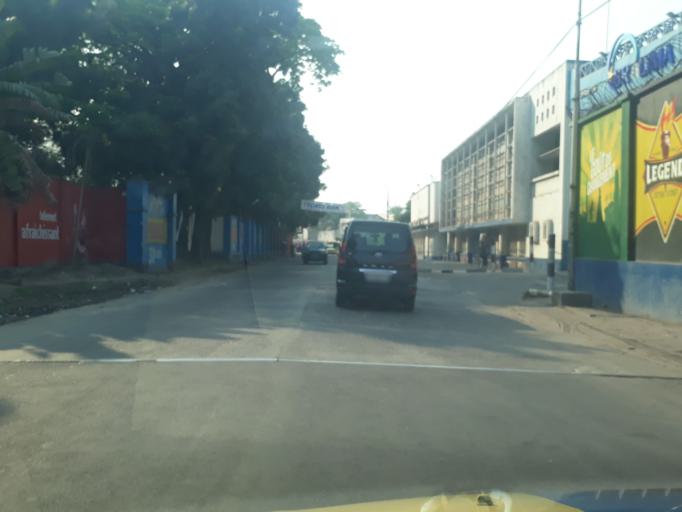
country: CD
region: Kinshasa
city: Kinshasa
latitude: -4.3082
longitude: 15.3265
